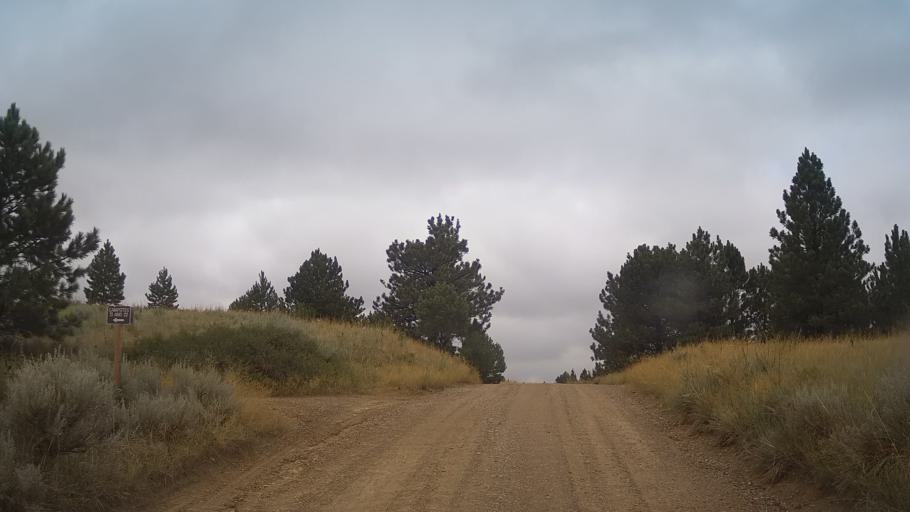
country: US
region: Montana
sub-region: Dawson County
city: Glendive
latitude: 47.0571
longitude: -104.6814
